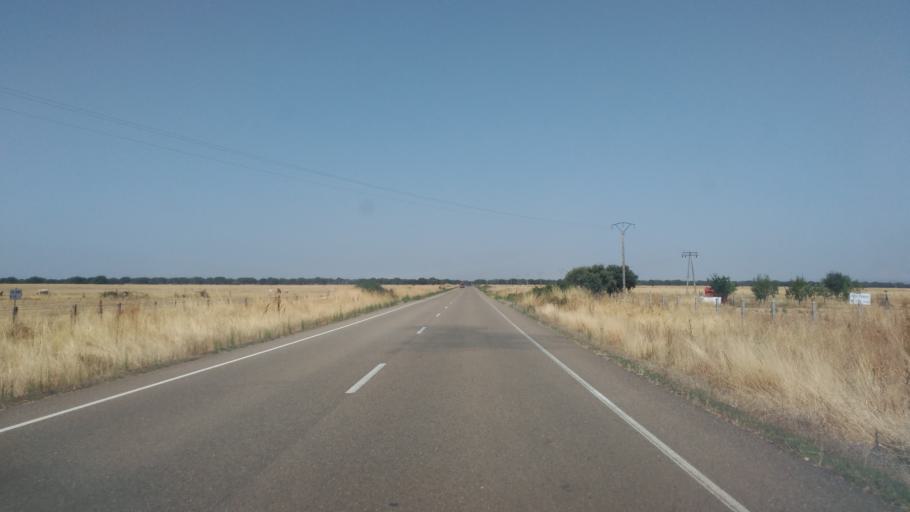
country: ES
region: Castille and Leon
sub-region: Provincia de Salamanca
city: Tamames
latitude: 40.6717
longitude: -6.1208
